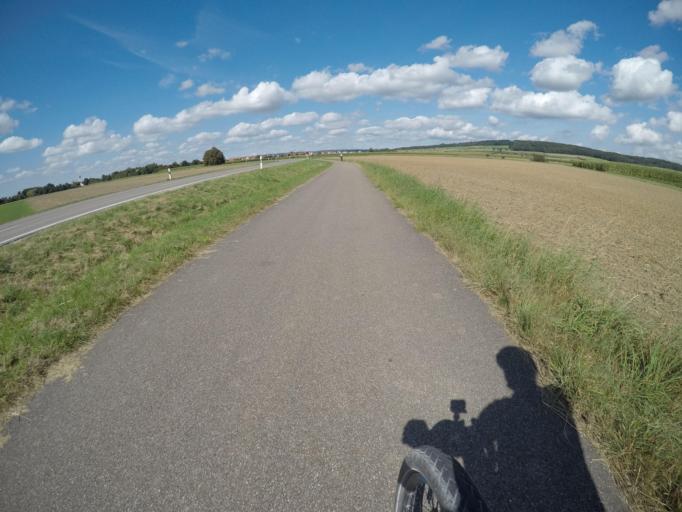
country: DE
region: Bavaria
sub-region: Swabia
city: Lutzingen
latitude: 48.6222
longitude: 10.5268
